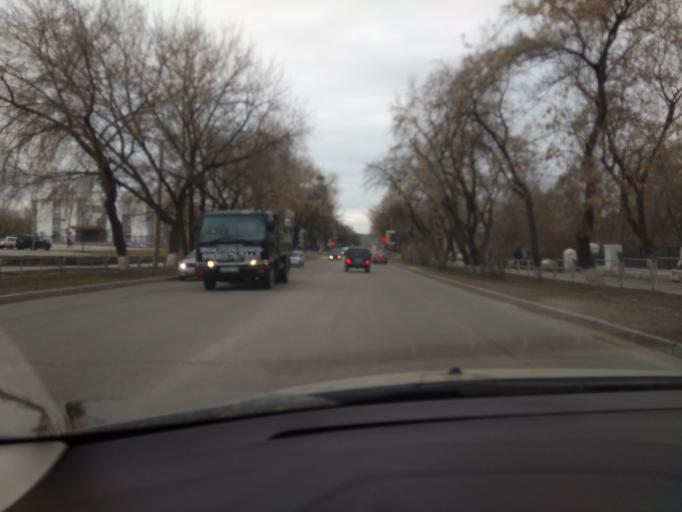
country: RU
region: Chelyabinsk
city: Kyshtym
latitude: 55.7064
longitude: 60.5558
